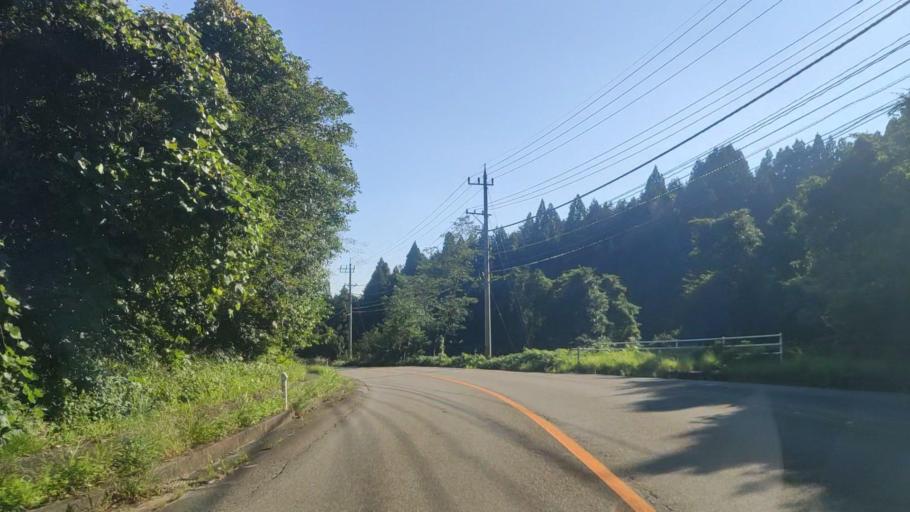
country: JP
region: Ishikawa
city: Nanao
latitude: 37.1227
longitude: 136.8624
